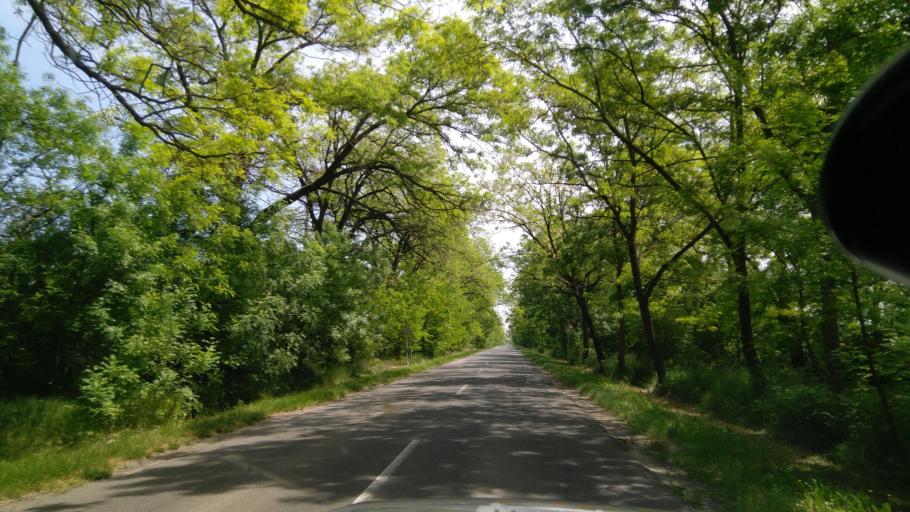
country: HU
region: Csongrad
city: Fabiansebestyen
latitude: 46.5756
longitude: 20.4508
